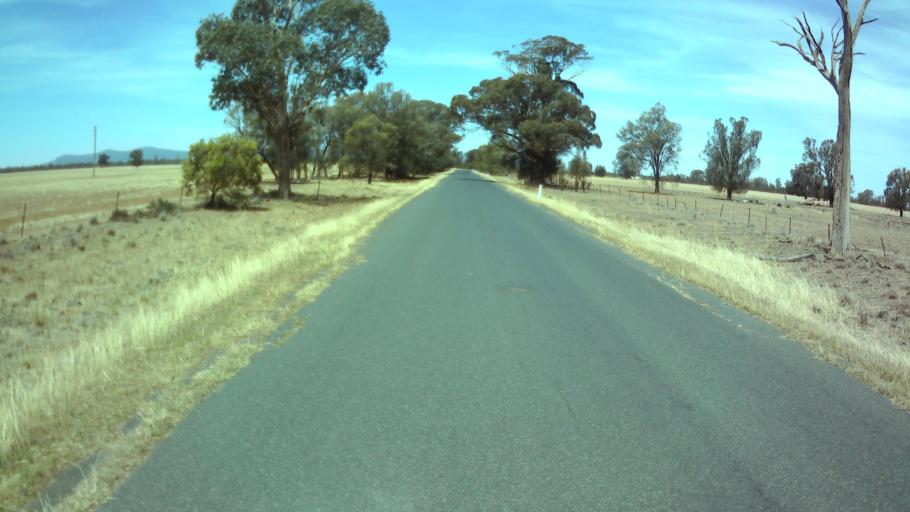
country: AU
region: New South Wales
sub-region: Weddin
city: Grenfell
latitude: -33.9412
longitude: 147.7704
